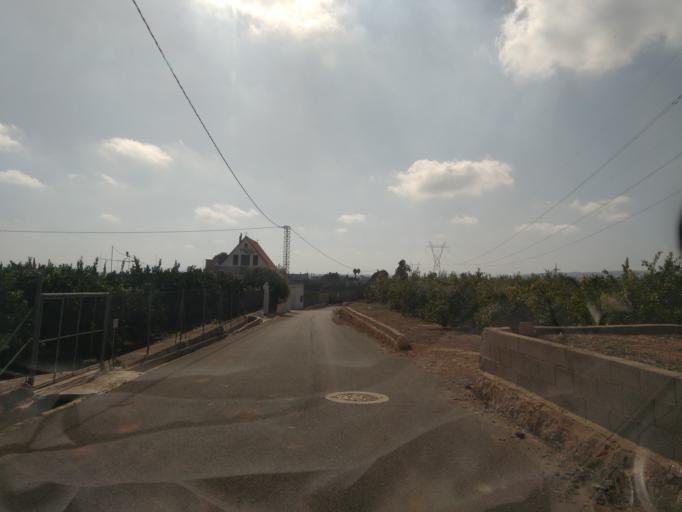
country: ES
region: Valencia
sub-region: Provincia de Valencia
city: Benimodo
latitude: 39.1773
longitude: -0.5513
